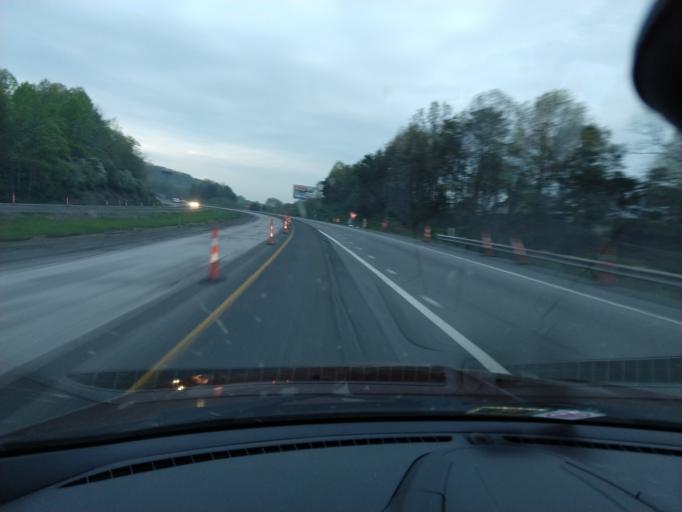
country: US
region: West Virginia
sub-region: Braxton County
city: Sutton
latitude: 38.7089
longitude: -80.6587
